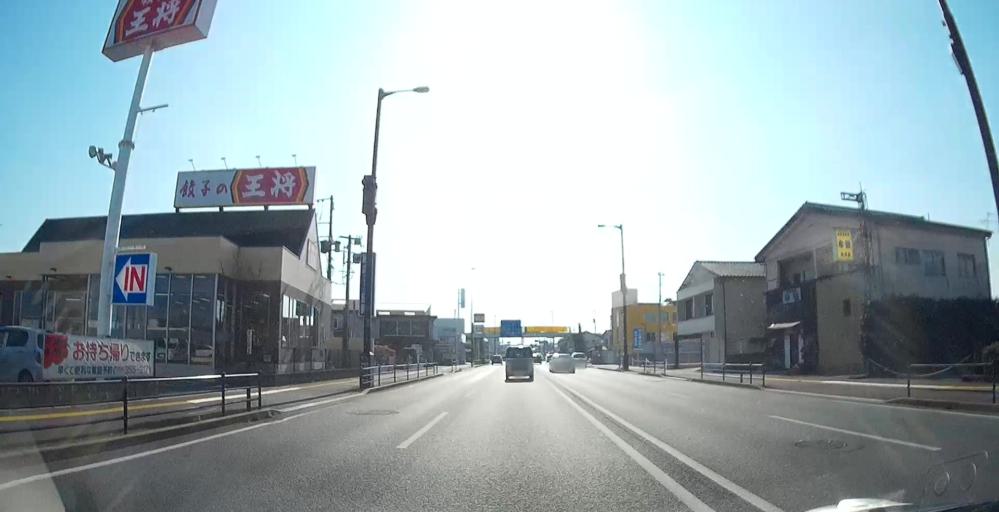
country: JP
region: Kumamoto
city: Kumamoto
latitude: 32.7670
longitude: 130.6917
